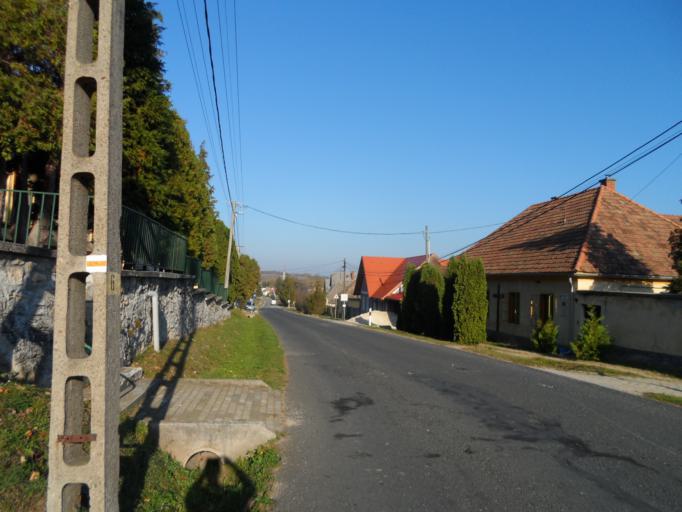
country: HU
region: Veszprem
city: Ajka
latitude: 47.2217
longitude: 17.6060
